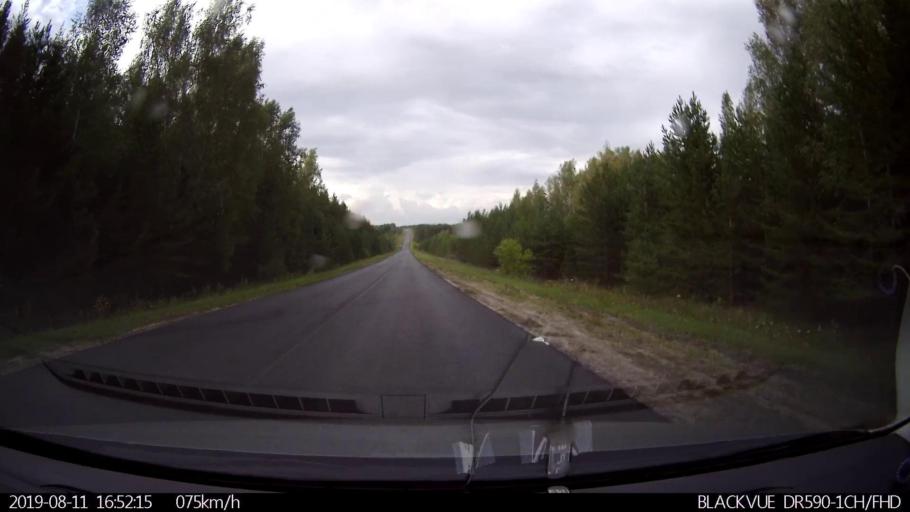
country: RU
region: Ulyanovsk
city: Mayna
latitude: 54.2456
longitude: 47.6748
